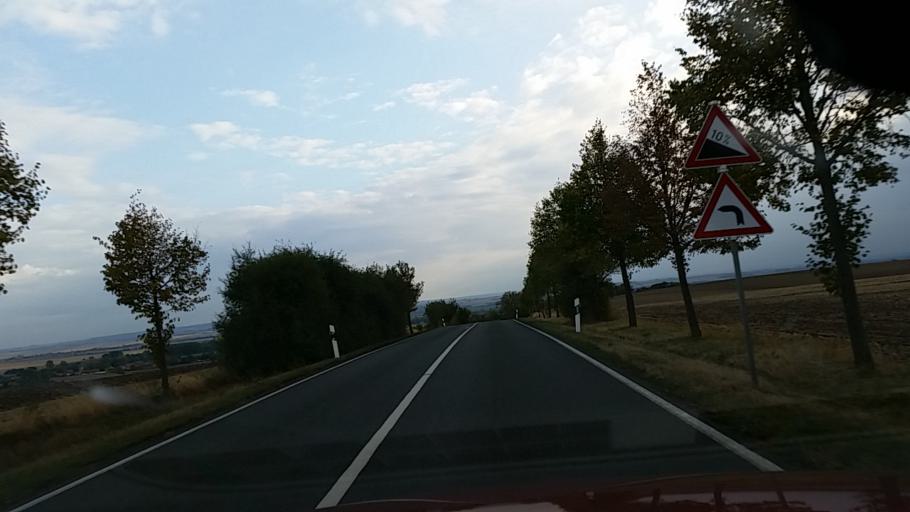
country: DE
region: Thuringia
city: Beichlingen
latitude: 51.2215
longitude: 11.2533
